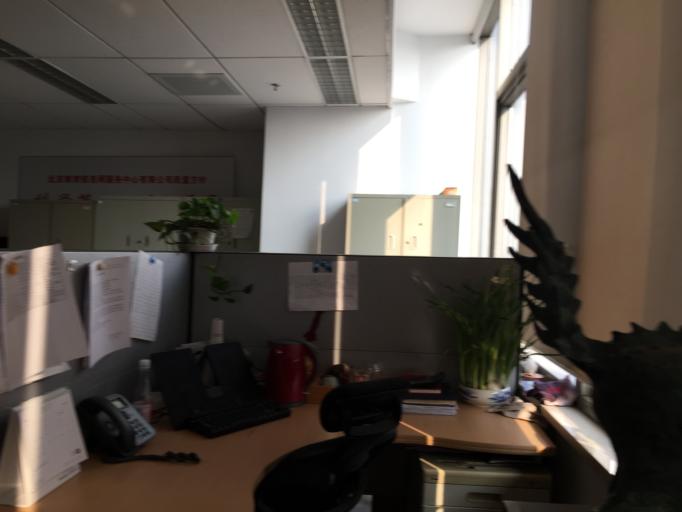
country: CN
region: Beijing
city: Qinghe
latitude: 39.9773
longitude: 116.3472
